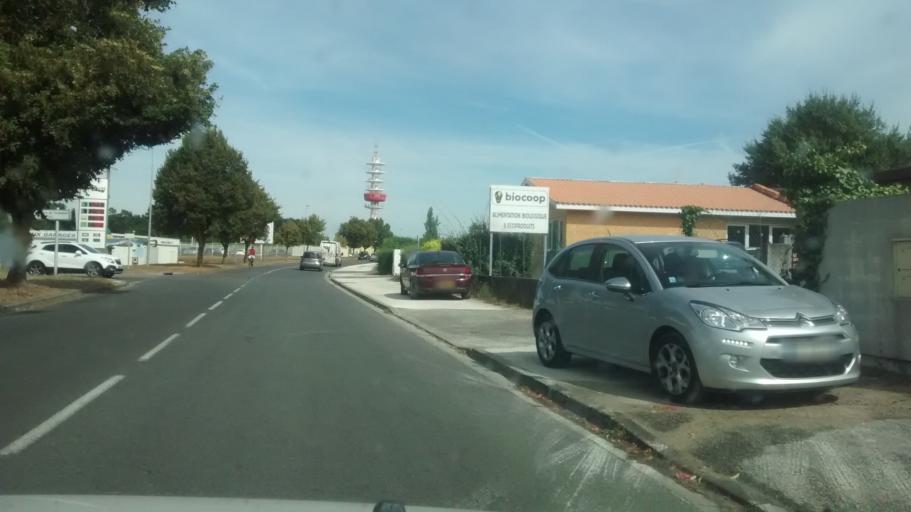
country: FR
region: Aquitaine
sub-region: Departement de la Gironde
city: Artigues-pres-Bordeaux
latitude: 44.8464
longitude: -0.4970
